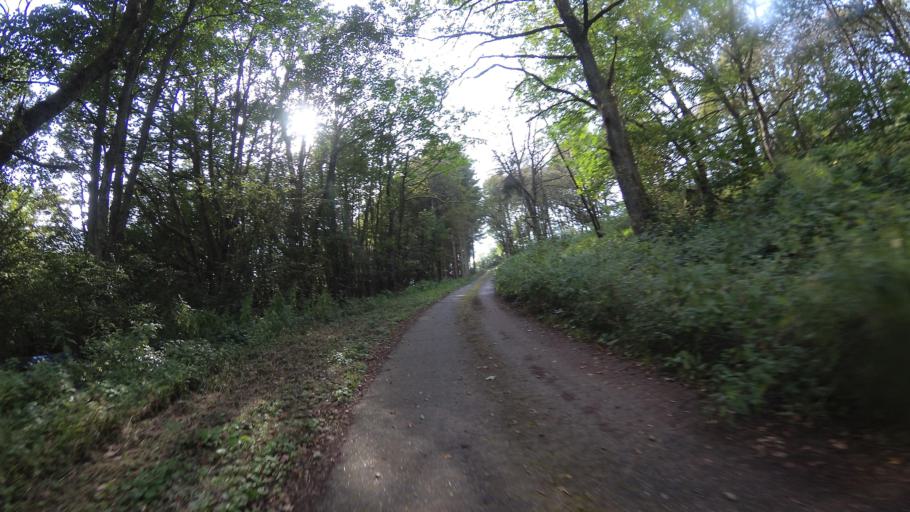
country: DE
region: Rheinland-Pfalz
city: Herchweiler
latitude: 49.4975
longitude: 7.2435
